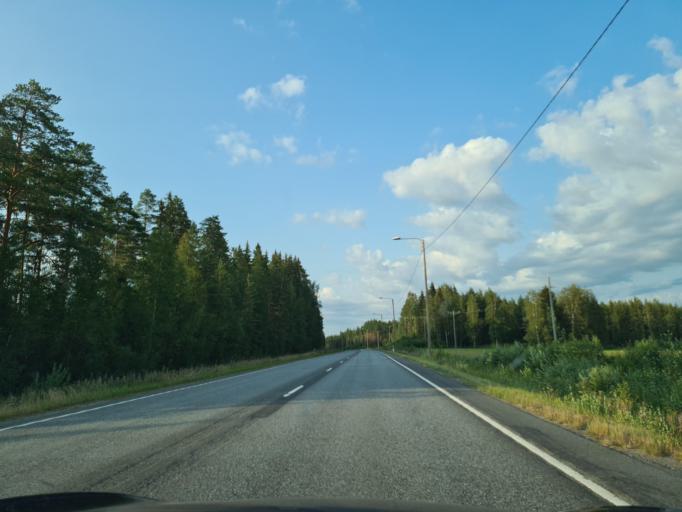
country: FI
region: Southern Ostrobothnia
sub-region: Seinaejoki
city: Kauhava
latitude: 63.0706
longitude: 23.0501
